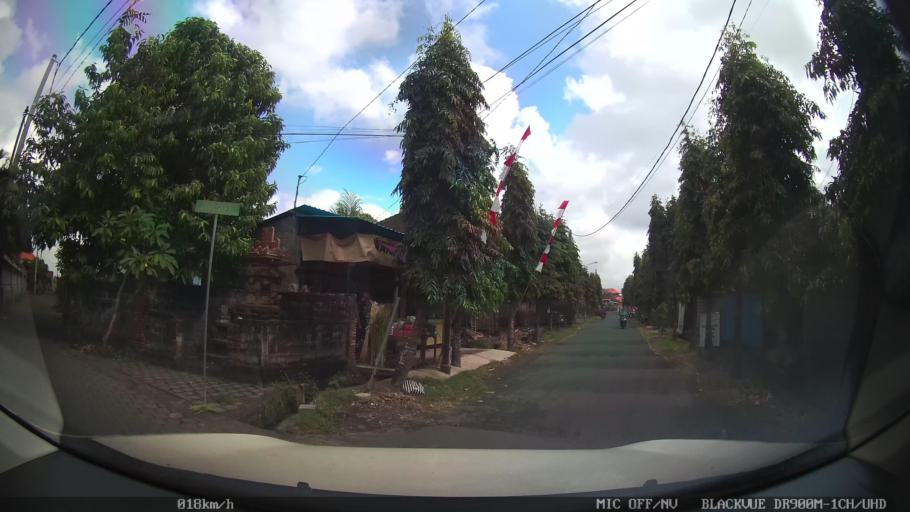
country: ID
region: Bali
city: Banjar Batur
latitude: -8.5944
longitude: 115.2102
